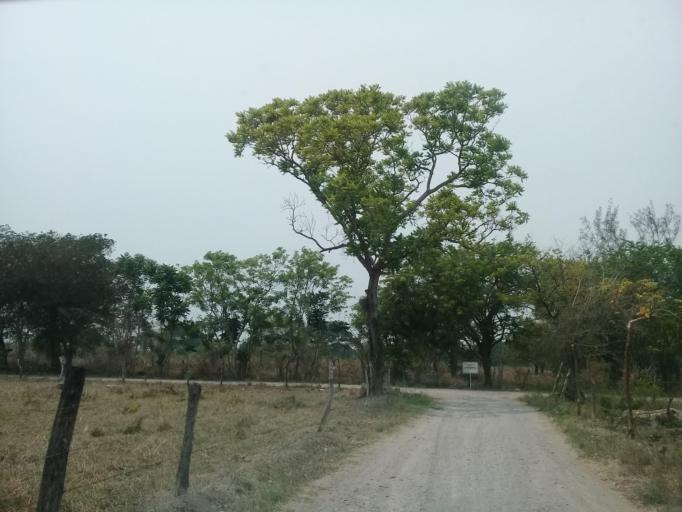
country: MX
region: Veracruz
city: Jamapa
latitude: 18.9333
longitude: -96.2056
